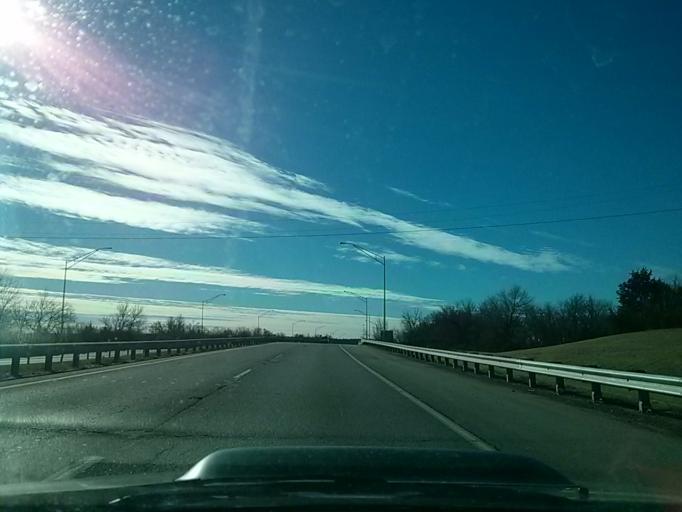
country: US
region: Oklahoma
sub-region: Tulsa County
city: Tulsa
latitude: 36.0981
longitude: -96.0071
